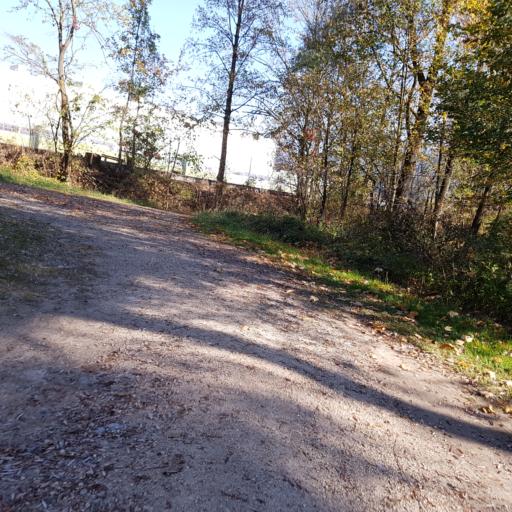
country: AT
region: Salzburg
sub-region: Politischer Bezirk Hallein
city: Hallein
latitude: 47.6720
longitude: 13.1117
